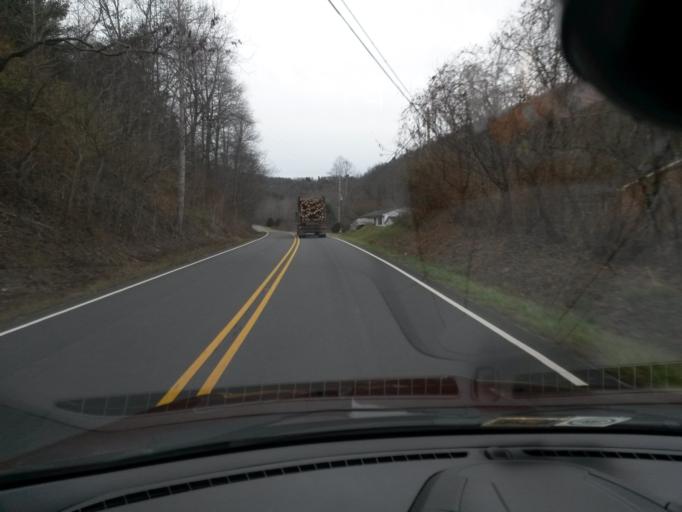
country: US
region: Virginia
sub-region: City of Buena Vista
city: Buena Vista
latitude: 37.6827
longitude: -79.2249
